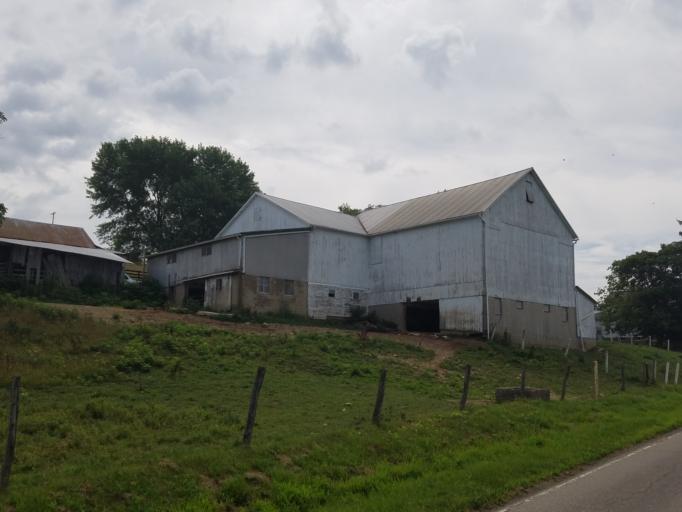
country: US
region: Ohio
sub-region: Tuscarawas County
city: Sugarcreek
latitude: 40.4225
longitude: -81.7489
